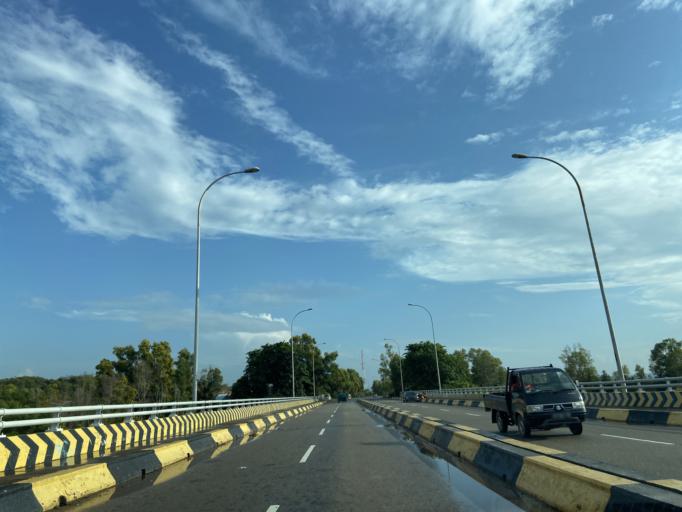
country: SG
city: Singapore
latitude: 0.9679
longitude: 104.0553
